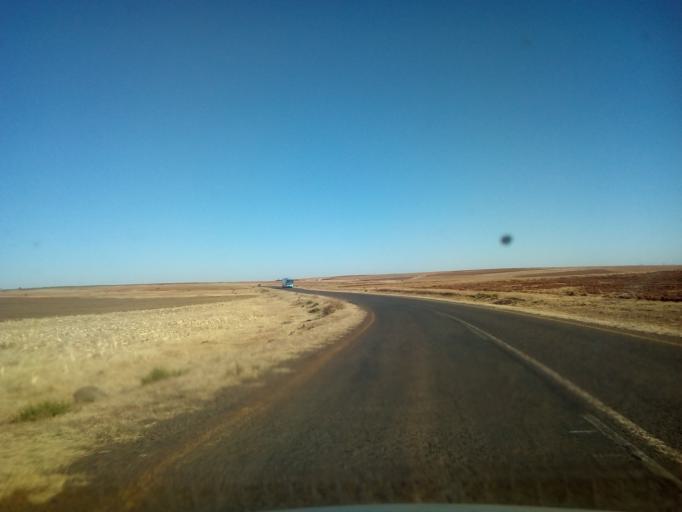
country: LS
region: Berea
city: Teyateyaneng
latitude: -29.2816
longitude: 27.6693
